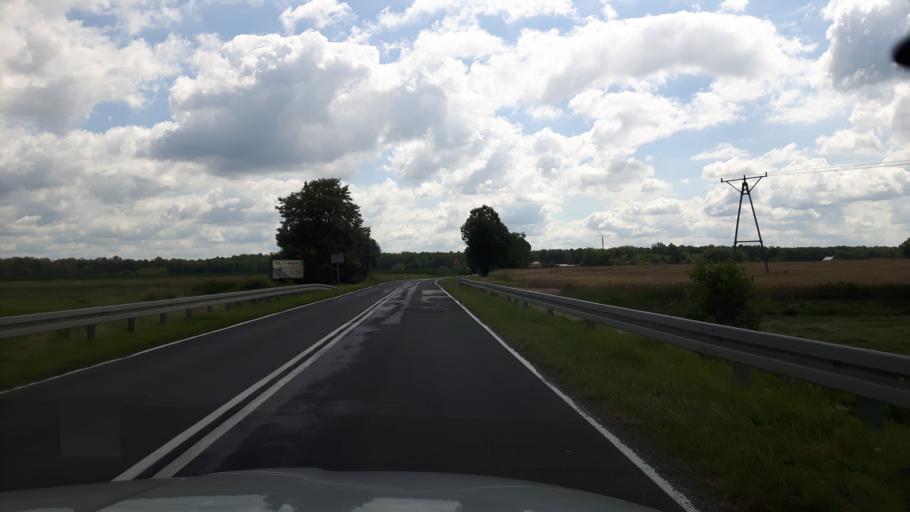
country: PL
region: Masovian Voivodeship
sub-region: Powiat ostrowski
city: Brok
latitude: 52.7028
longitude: 21.9064
